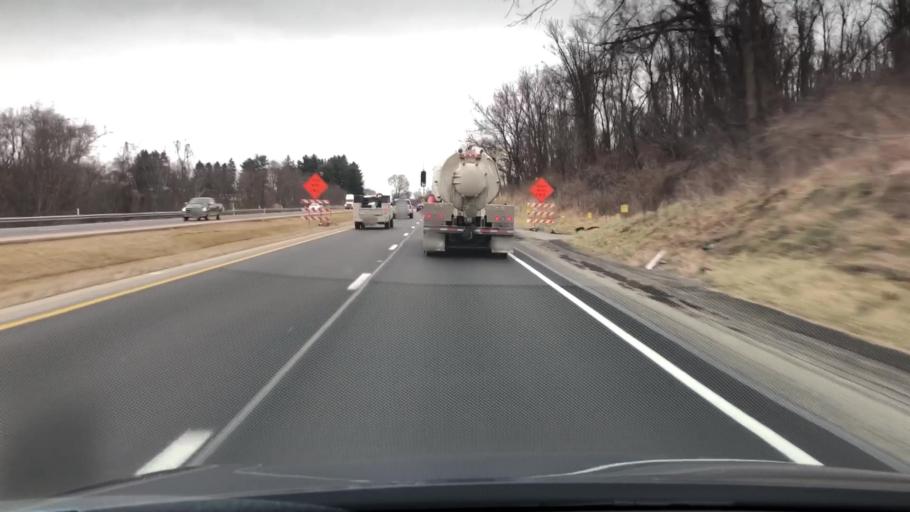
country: US
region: Pennsylvania
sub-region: Washington County
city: East Washington
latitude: 40.1446
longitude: -80.2060
